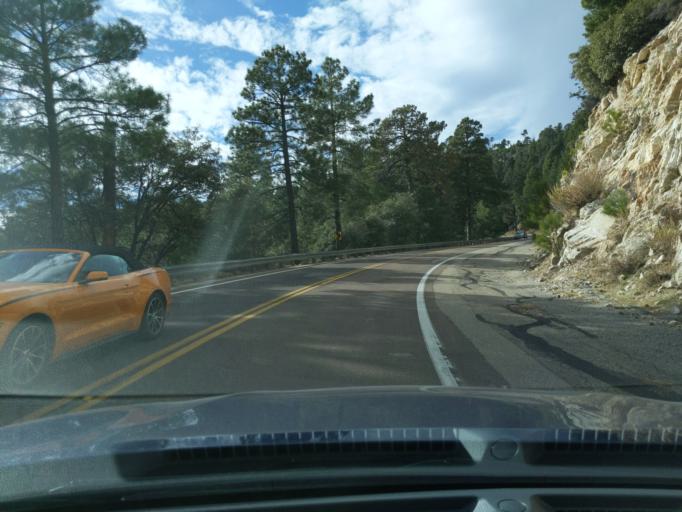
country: US
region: Arizona
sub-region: Pima County
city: Tanque Verde
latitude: 32.4096
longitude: -110.7066
